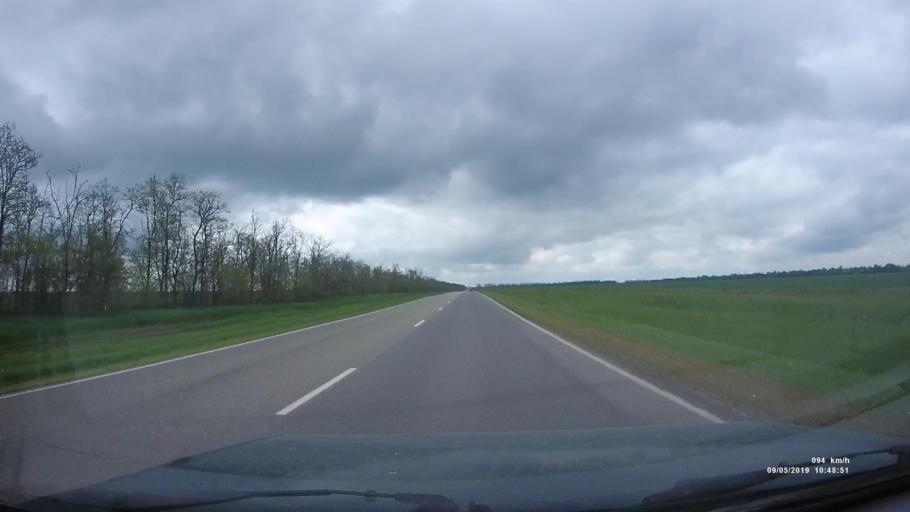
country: RU
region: Rostov
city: Peshkovo
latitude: 46.9509
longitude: 39.3559
